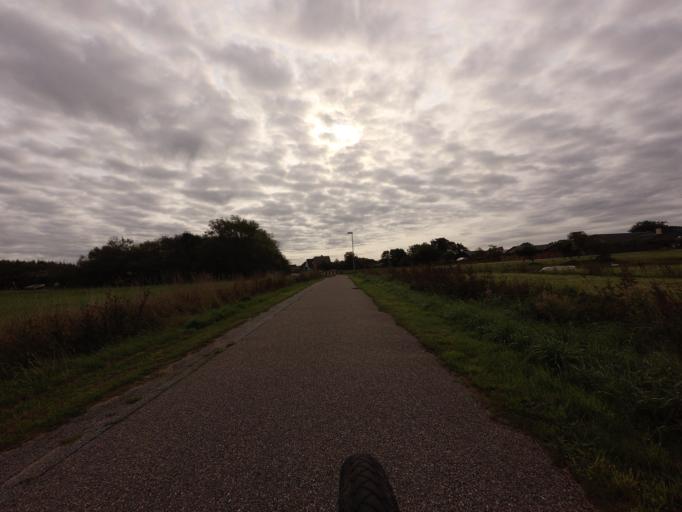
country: DK
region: North Denmark
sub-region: Hjorring Kommune
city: Hirtshals
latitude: 57.5638
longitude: 10.0217
